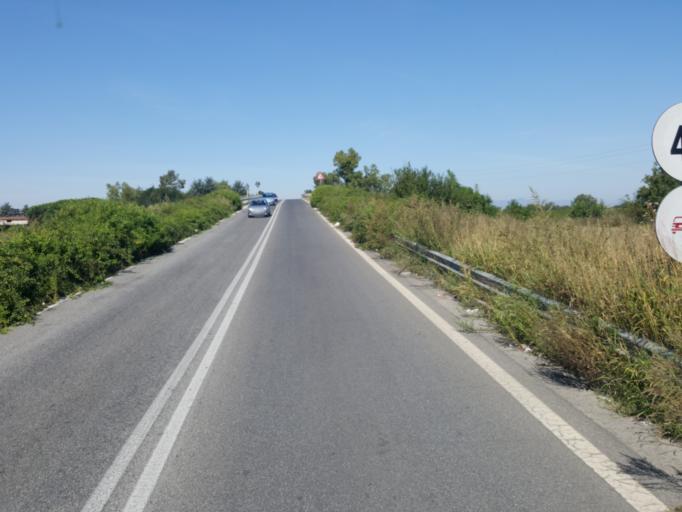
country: IT
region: Campania
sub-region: Provincia di Napoli
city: Pascarola
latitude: 40.9672
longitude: 14.2946
